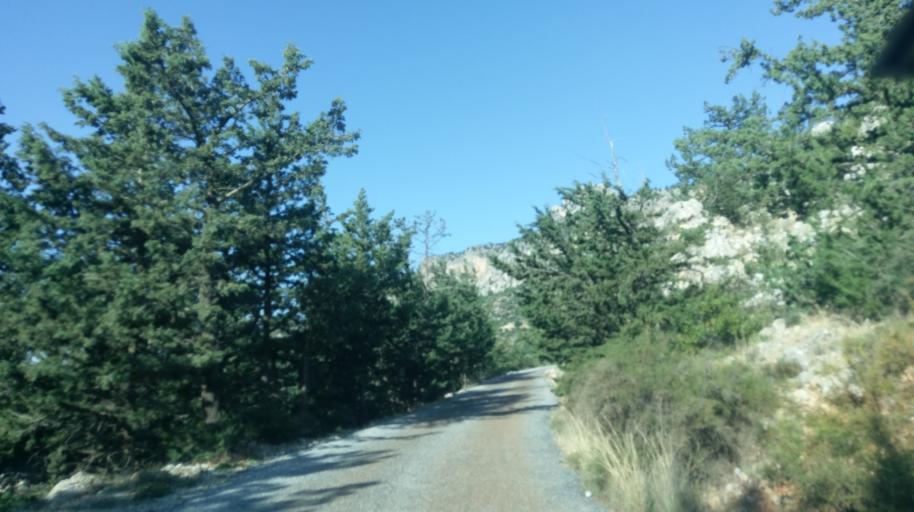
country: CY
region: Keryneia
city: Kyrenia
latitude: 35.2799
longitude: 33.4205
